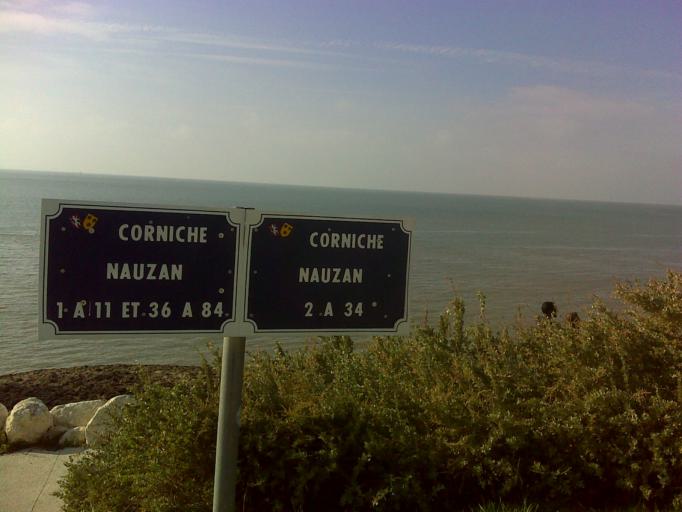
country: FR
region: Poitou-Charentes
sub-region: Departement de la Charente-Maritime
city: Saint-Palais-sur-Mer
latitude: 45.6375
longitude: -1.0839
